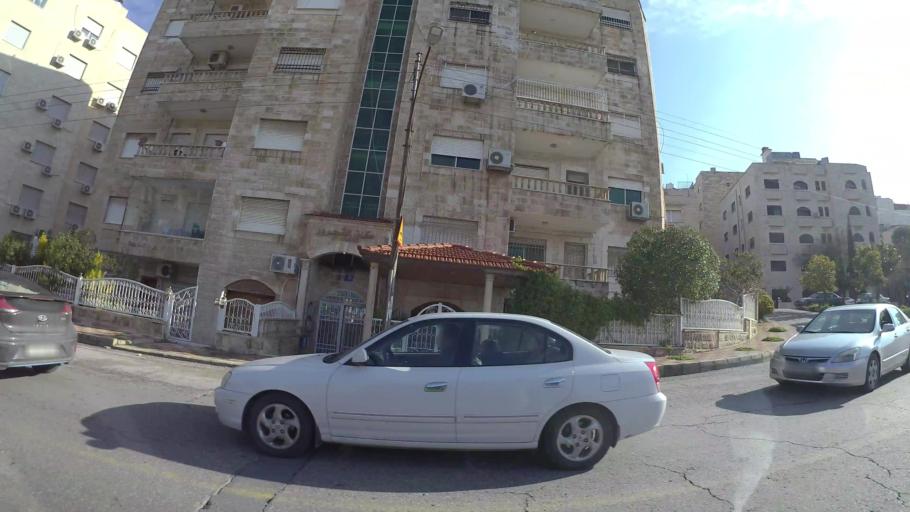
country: JO
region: Amman
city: Al Jubayhah
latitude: 32.0035
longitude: 35.8821
